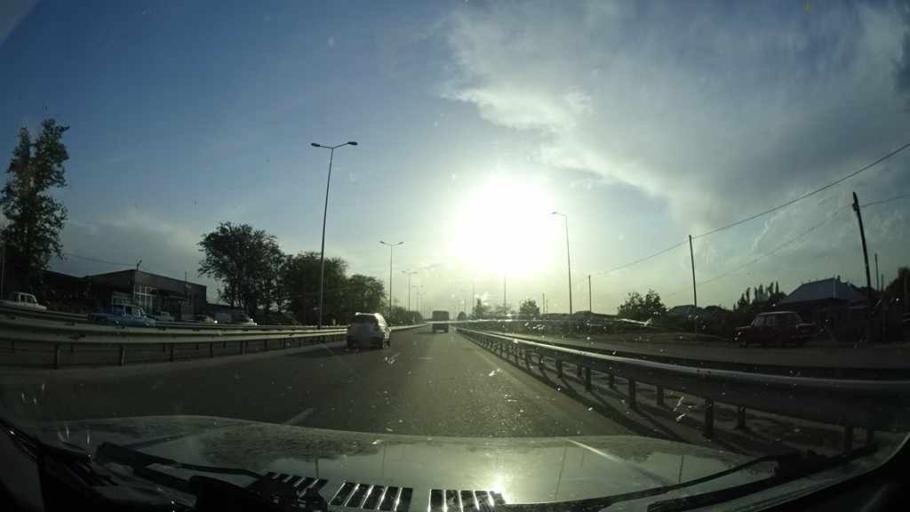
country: AZ
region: Samux
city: Samux
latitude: 40.6892
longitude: 46.5560
